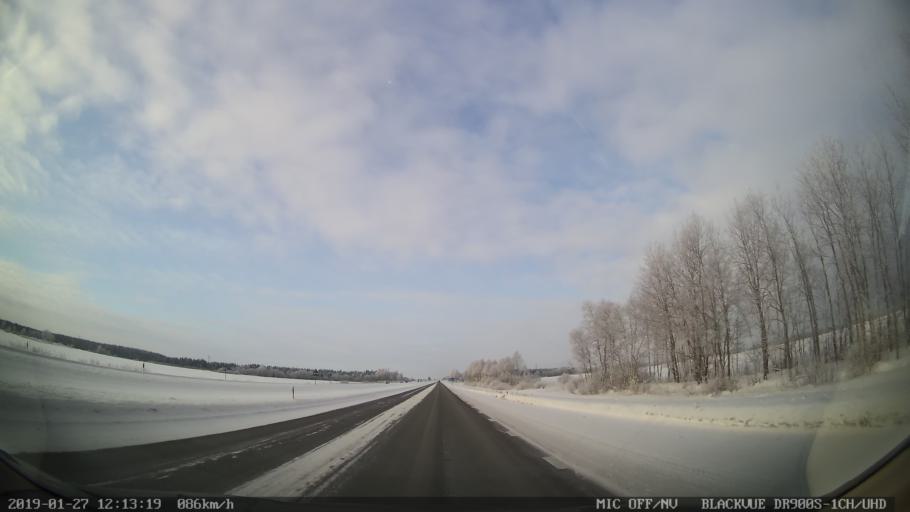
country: EE
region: Harju
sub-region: Raasiku vald
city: Raasiku
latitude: 59.4364
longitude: 25.1619
